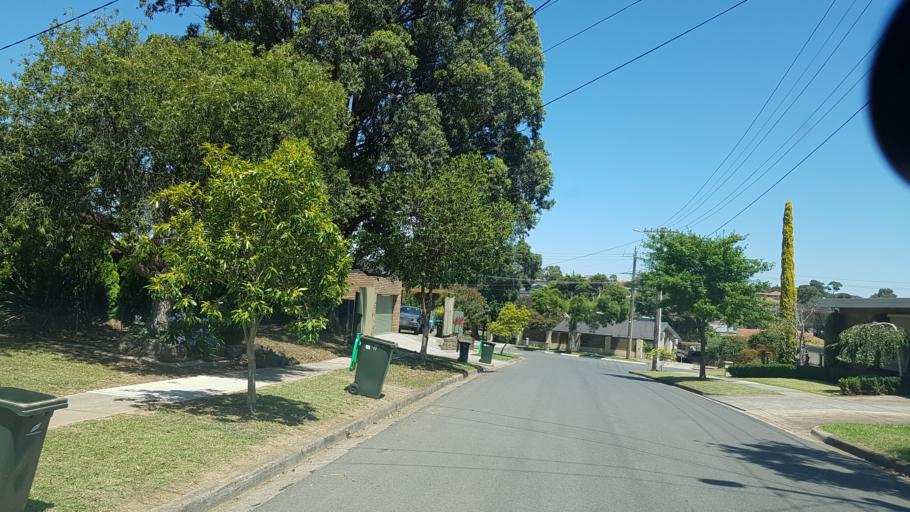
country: AU
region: Victoria
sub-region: Manningham
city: Bulleen
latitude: -37.7580
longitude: 145.0950
